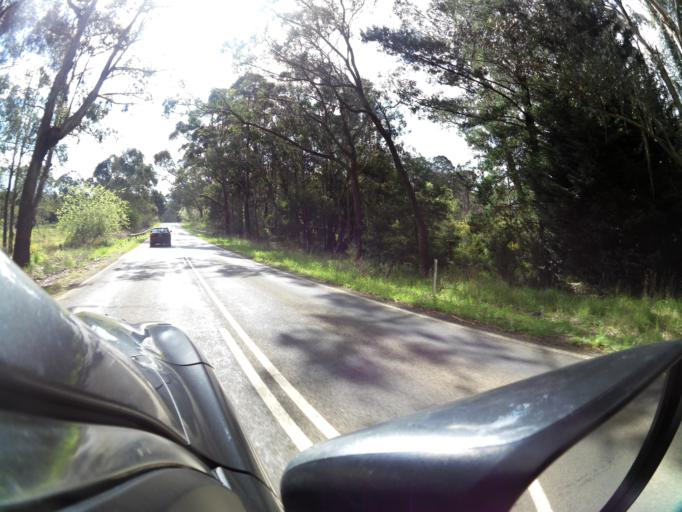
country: AU
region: Victoria
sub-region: Mount Alexander
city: Castlemaine
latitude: -37.3942
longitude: 144.2206
